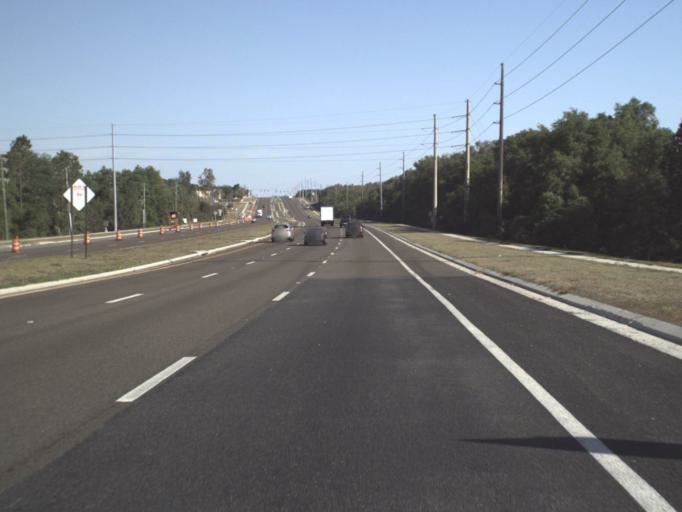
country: US
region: Florida
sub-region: Lake County
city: Clermont
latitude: 28.4912
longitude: -81.7156
